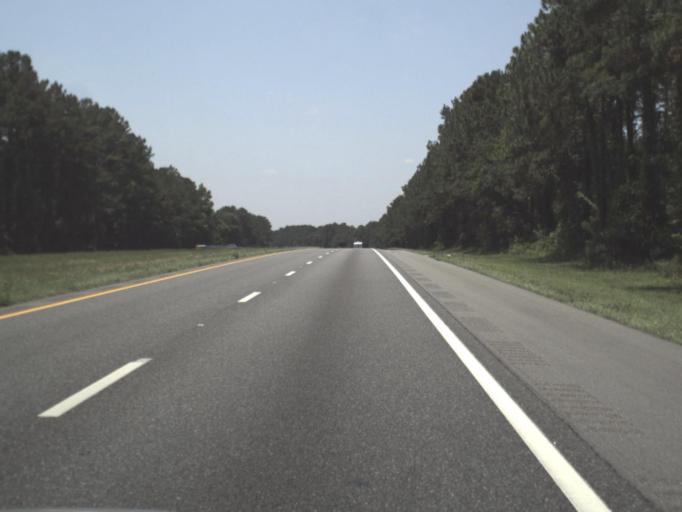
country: US
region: Florida
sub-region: Suwannee County
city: Wellborn
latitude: 30.2607
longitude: -82.7313
